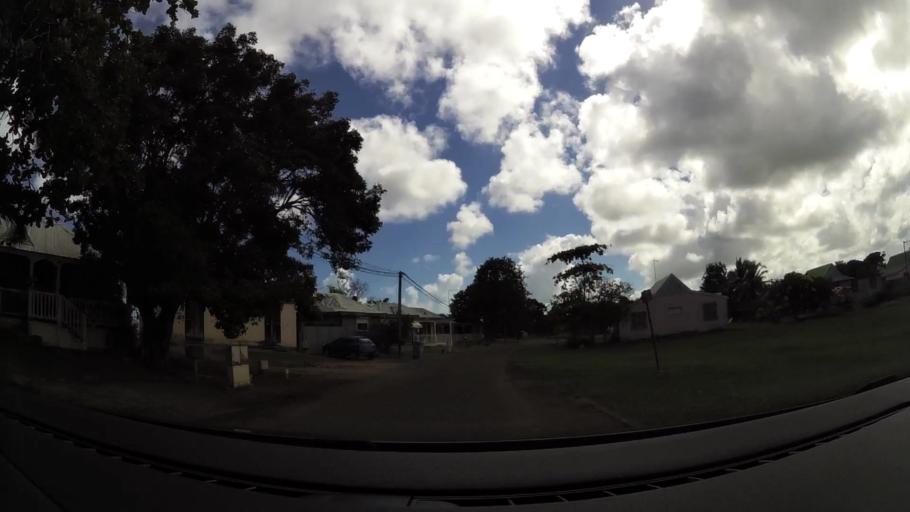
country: GP
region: Guadeloupe
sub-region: Guadeloupe
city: Anse-Bertrand
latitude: 16.4657
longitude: -61.5037
